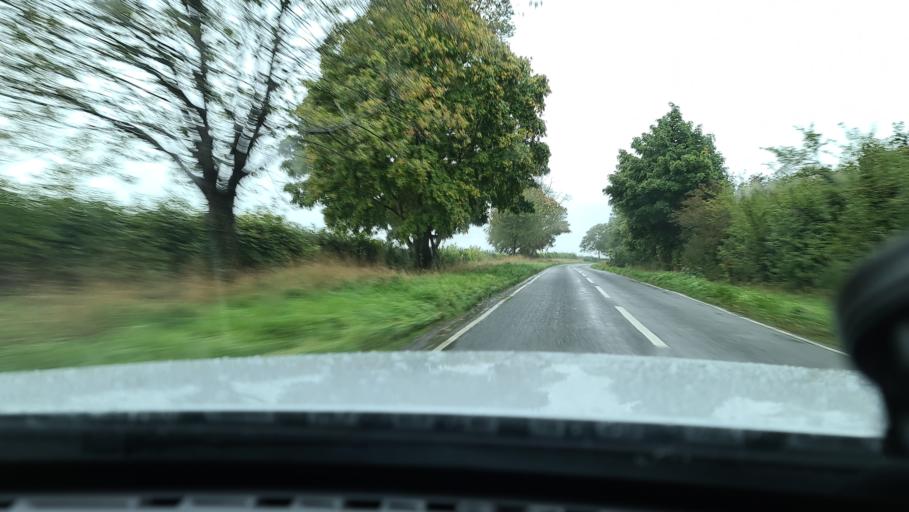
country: GB
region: England
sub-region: Oxfordshire
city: Woodstock
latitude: 51.8818
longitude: -1.3665
